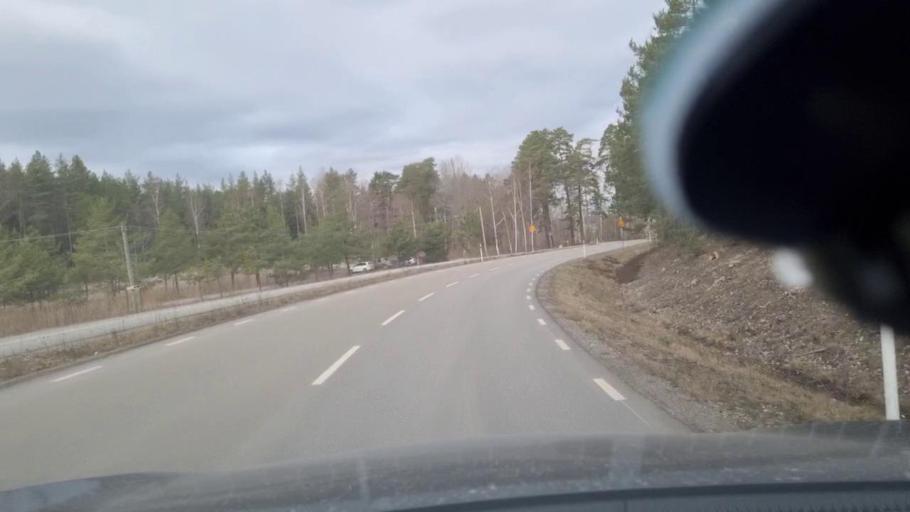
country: SE
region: Stockholm
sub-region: Upplands-Bro Kommun
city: Kungsaengen
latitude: 59.4238
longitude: 17.7735
